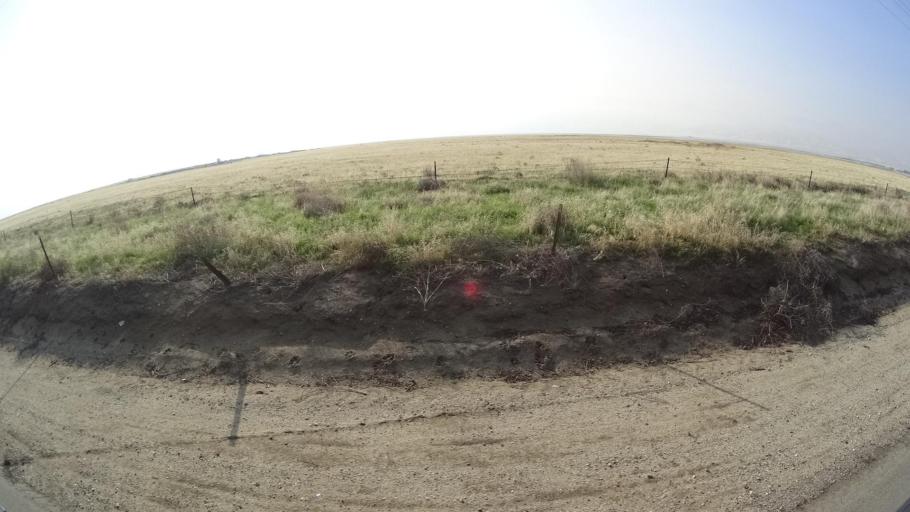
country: US
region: California
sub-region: Kern County
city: Lebec
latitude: 34.9844
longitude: -118.9202
